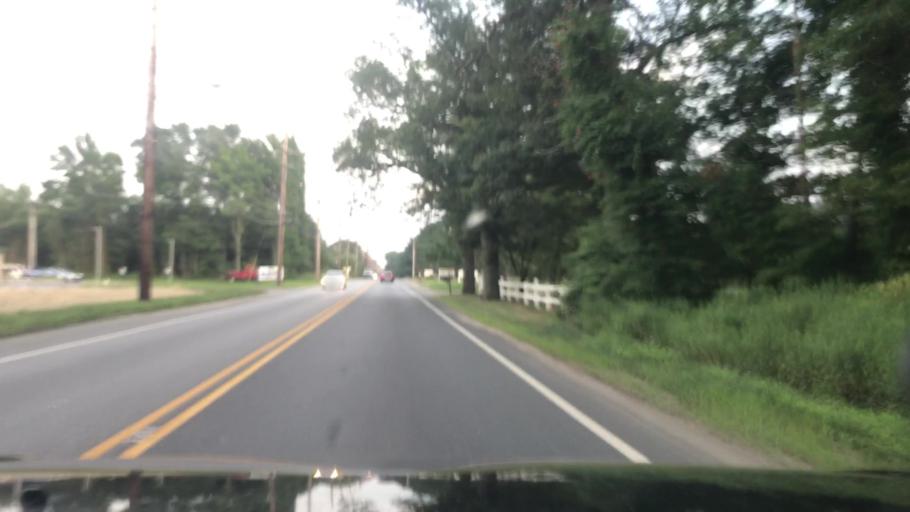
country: US
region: New Jersey
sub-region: Ocean County
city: Lakewood
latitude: 40.0707
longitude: -74.2442
